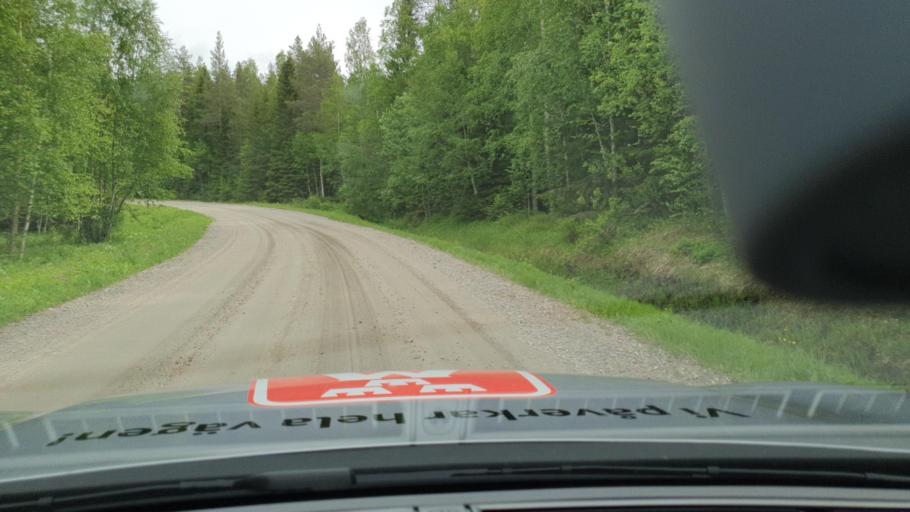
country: FI
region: Lapland
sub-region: Torniolaakso
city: Ylitornio
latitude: 65.9438
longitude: 23.5450
